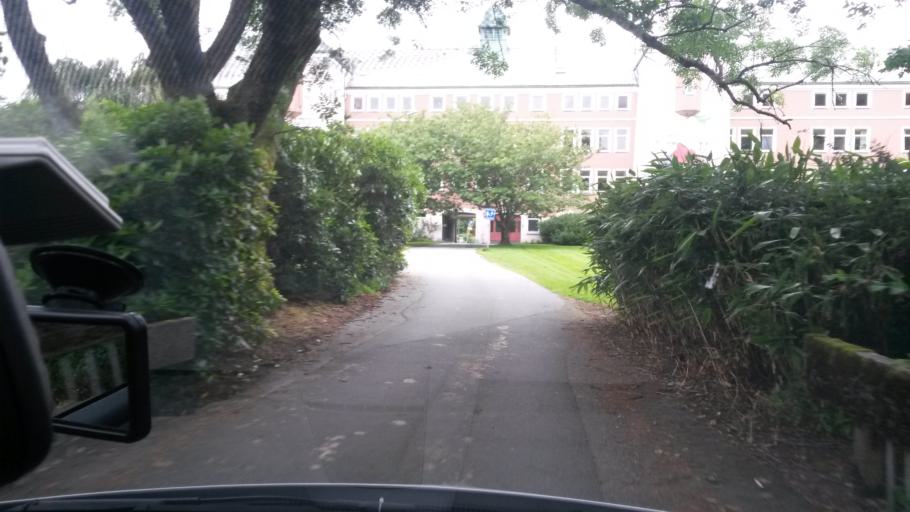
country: NO
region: Rogaland
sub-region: Sandnes
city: Sandnes
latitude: 58.8999
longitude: 5.7800
